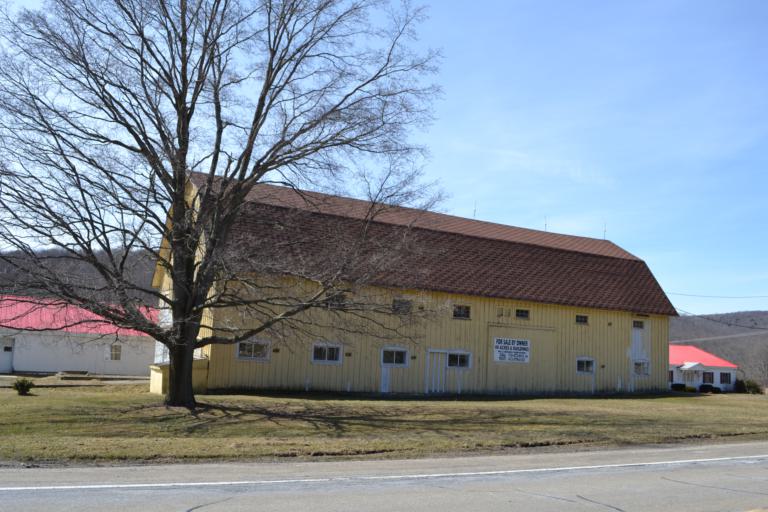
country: US
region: New York
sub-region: Cattaraugus County
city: Franklinville
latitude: 42.2820
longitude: -78.4506
